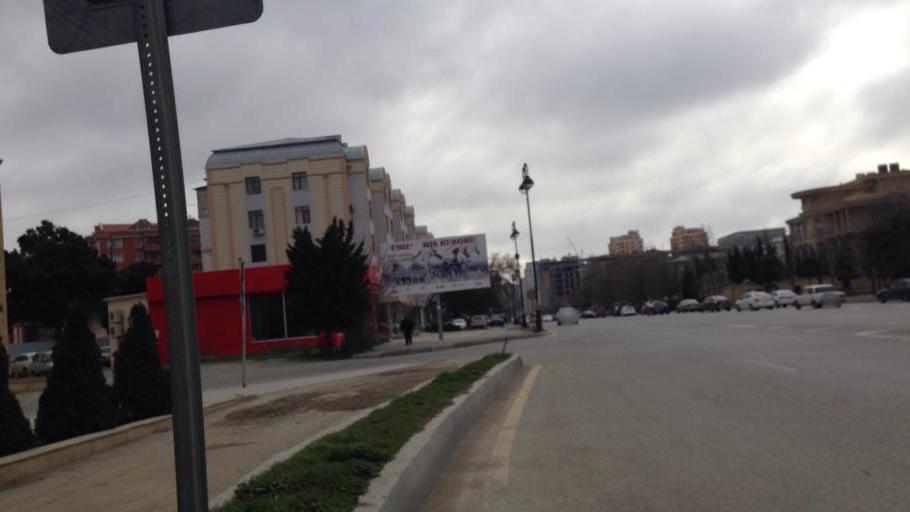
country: AZ
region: Baki
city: Bilajari
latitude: 40.4073
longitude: 49.8358
